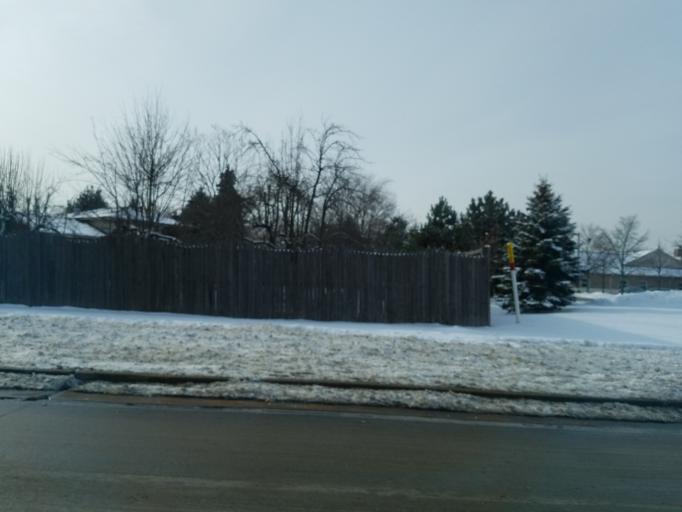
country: US
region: Illinois
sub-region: Cook County
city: Orland Hills
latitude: 41.6153
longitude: -87.8142
